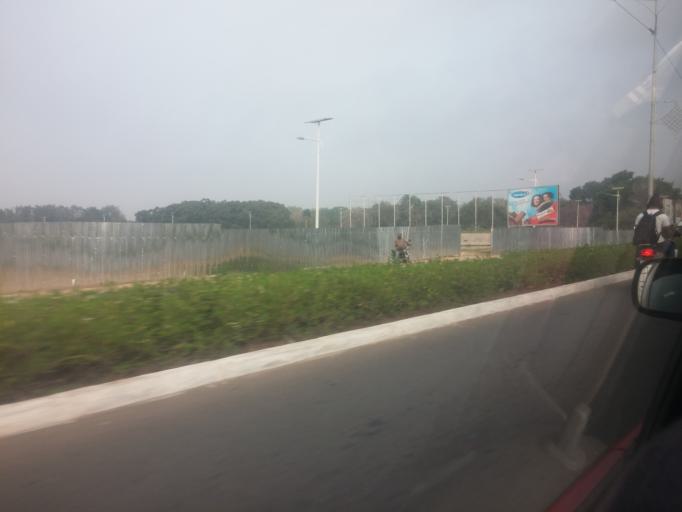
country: TG
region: Maritime
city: Lome
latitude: 6.1669
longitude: 1.2221
